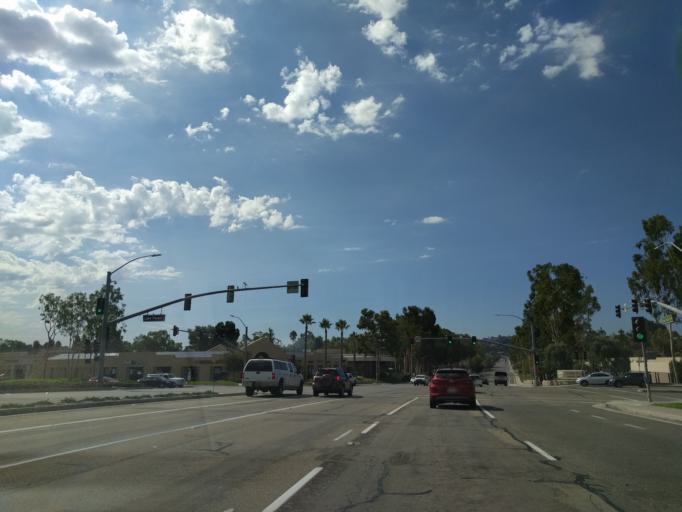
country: US
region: California
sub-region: Orange County
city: Laguna Woods
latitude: 33.6300
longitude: -117.7301
